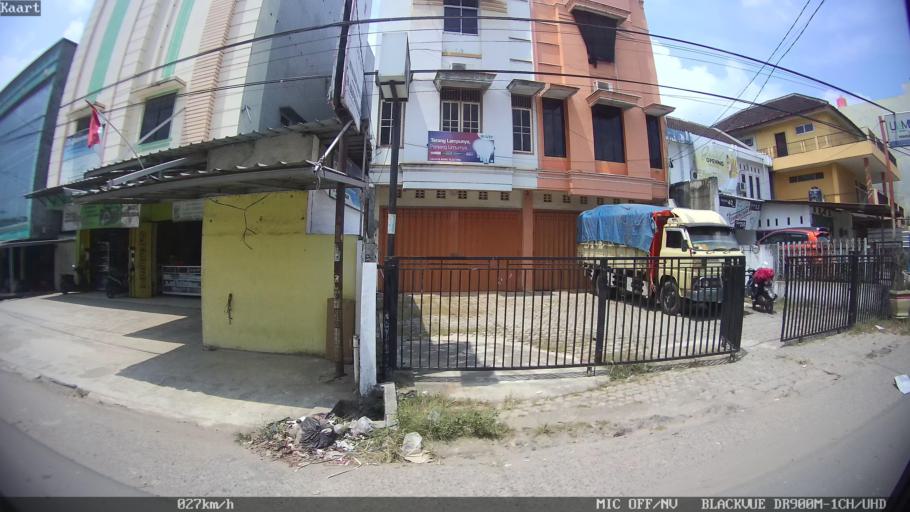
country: ID
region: Lampung
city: Pringsewu
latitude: -5.3557
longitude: 104.9750
